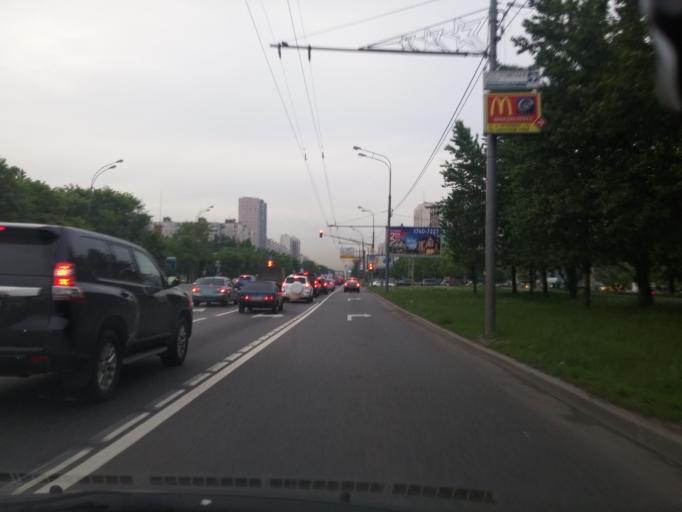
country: RU
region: Moscow
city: Altuf'yevskiy
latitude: 55.8862
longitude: 37.5870
